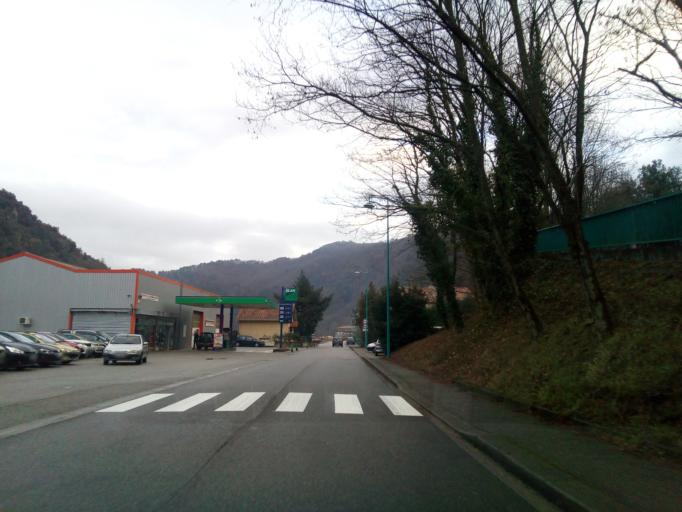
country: FR
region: Rhone-Alpes
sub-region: Departement de l'Ardeche
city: Saint-Sauveur-de-Montagut
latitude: 44.8191
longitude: 4.5920
